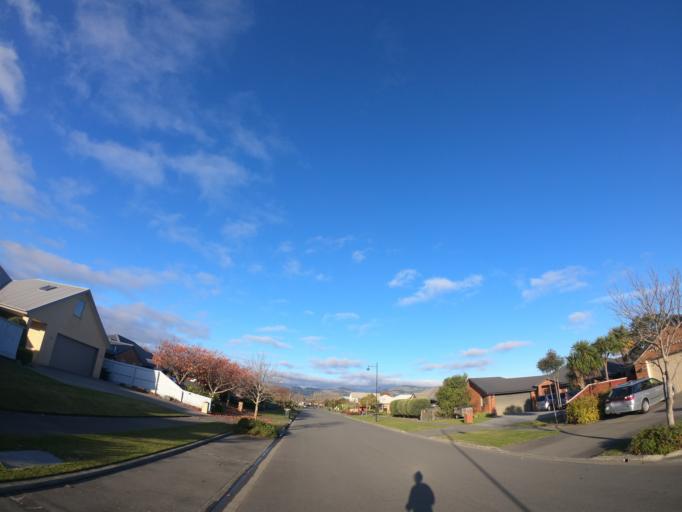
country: NZ
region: Canterbury
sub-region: Selwyn District
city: Prebbleton
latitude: -43.5674
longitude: 172.5676
